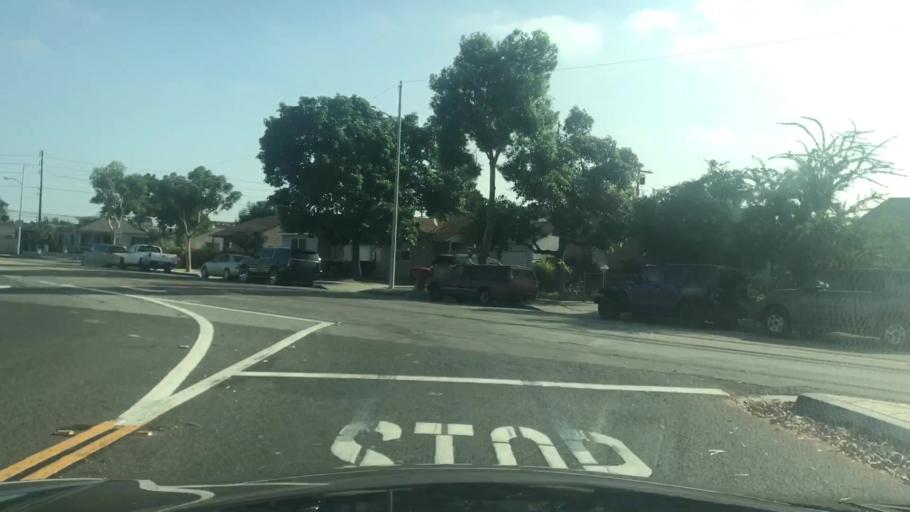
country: US
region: California
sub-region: Los Angeles County
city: Norwalk
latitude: 33.9004
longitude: -118.0555
